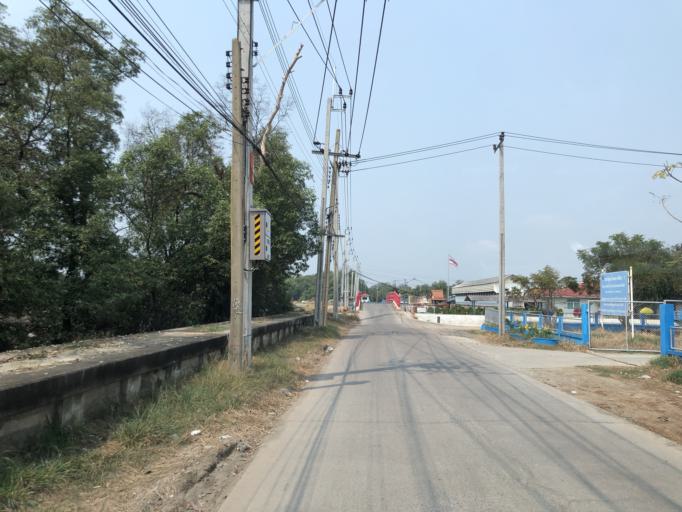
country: TH
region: Samut Prakan
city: Bang Bo
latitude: 13.5175
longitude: 100.8208
